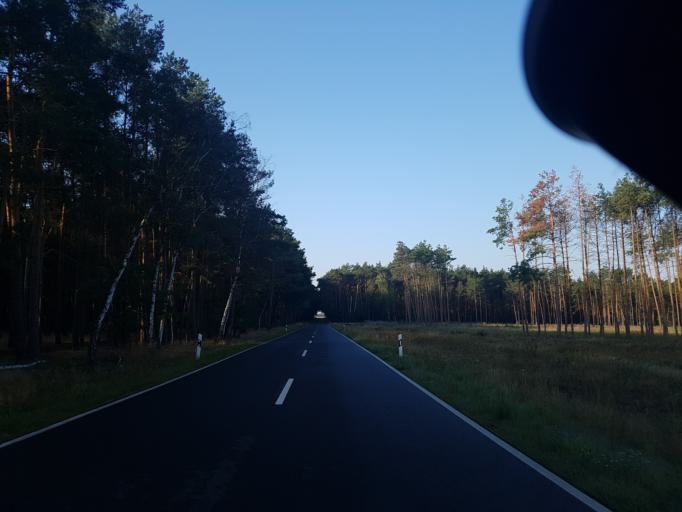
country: DE
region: Saxony-Anhalt
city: Holzdorf
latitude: 51.8034
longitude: 13.1369
